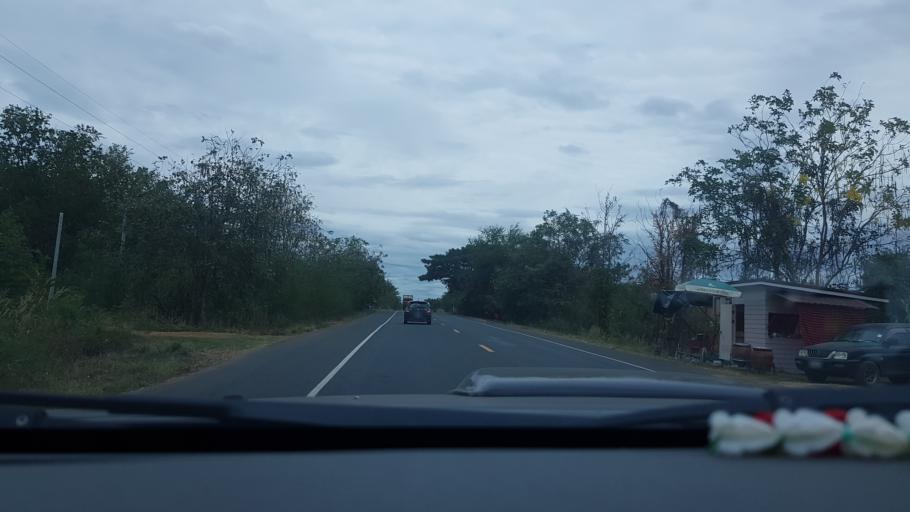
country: TH
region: Phetchabun
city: Phetchabun
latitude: 16.4661
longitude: 101.1244
